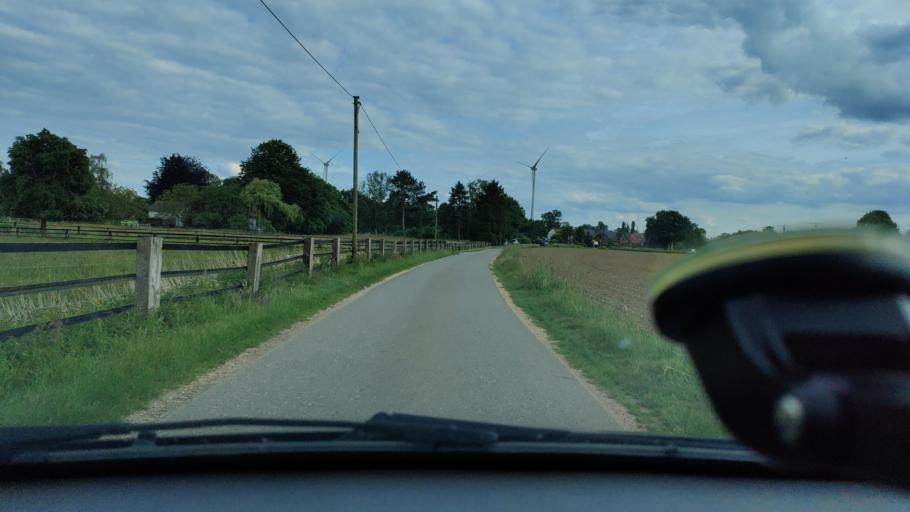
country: DE
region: North Rhine-Westphalia
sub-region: Regierungsbezirk Dusseldorf
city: Goch
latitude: 51.6710
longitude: 6.1962
